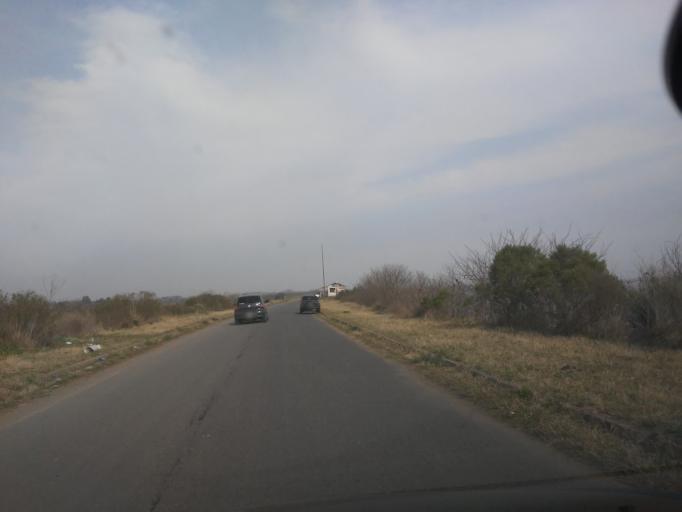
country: AR
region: Buenos Aires
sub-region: Partido de Marcos Paz
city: Marcos Paz
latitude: -34.6823
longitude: -58.8590
